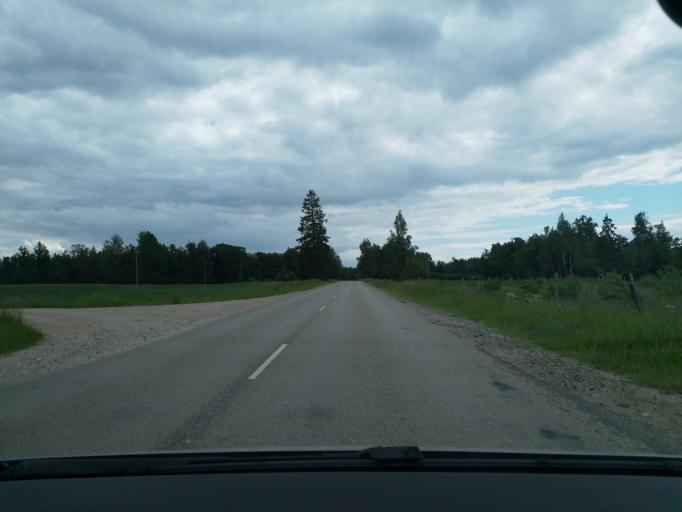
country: LV
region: Kuldigas Rajons
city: Kuldiga
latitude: 56.9258
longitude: 21.9274
